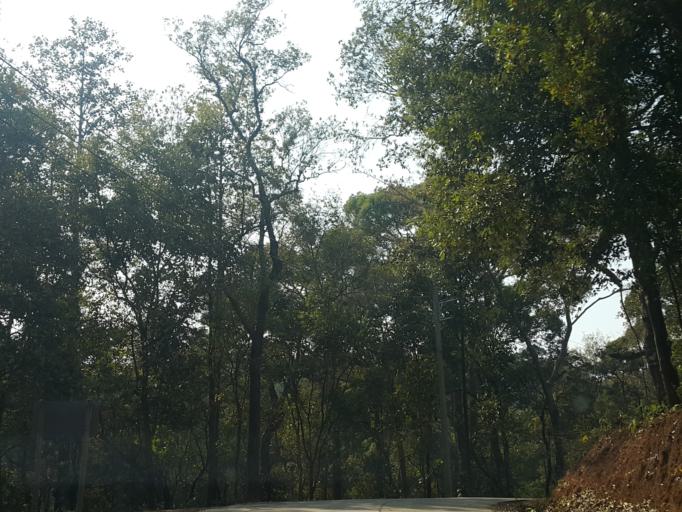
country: TH
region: Chiang Mai
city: Mae Taeng
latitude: 19.0216
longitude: 98.7977
